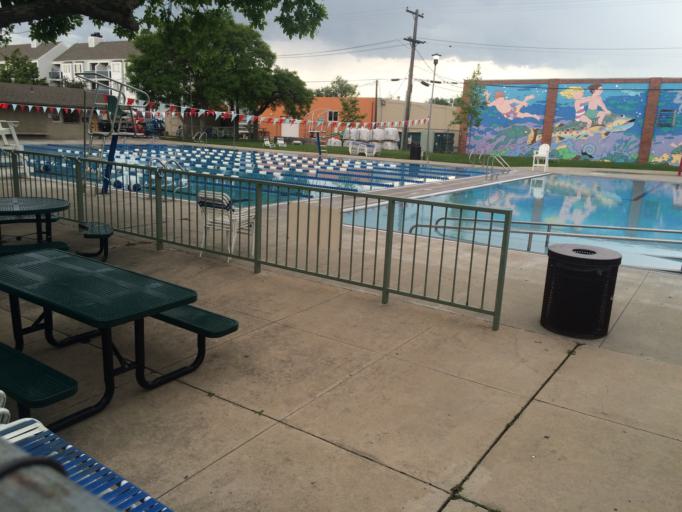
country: US
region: Colorado
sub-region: Boulder County
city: Boulder
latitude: 40.0212
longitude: -105.2682
